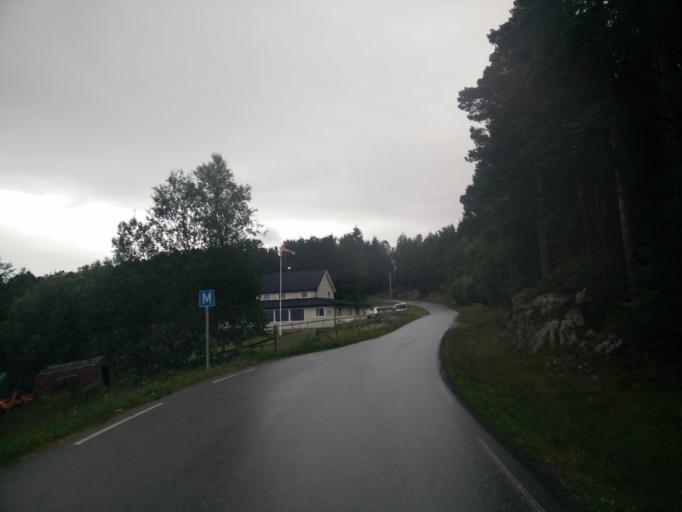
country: NO
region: More og Romsdal
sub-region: Kristiansund
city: Rensvik
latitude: 63.0205
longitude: 7.8985
